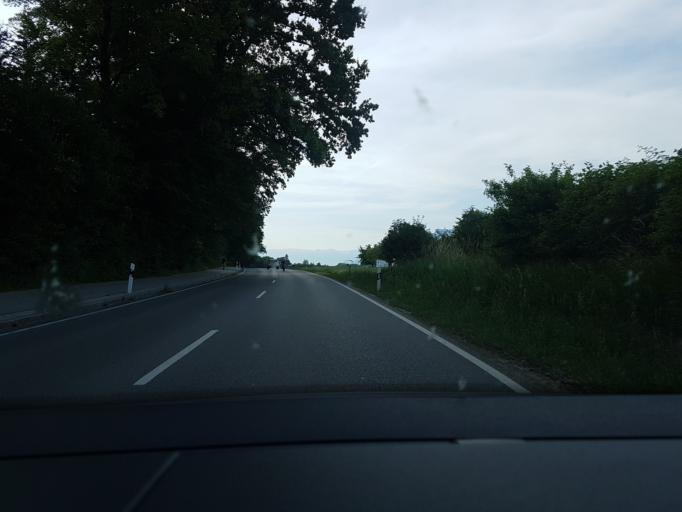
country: DE
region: Bavaria
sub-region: Upper Bavaria
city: Ainring
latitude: 47.8529
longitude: 12.9389
